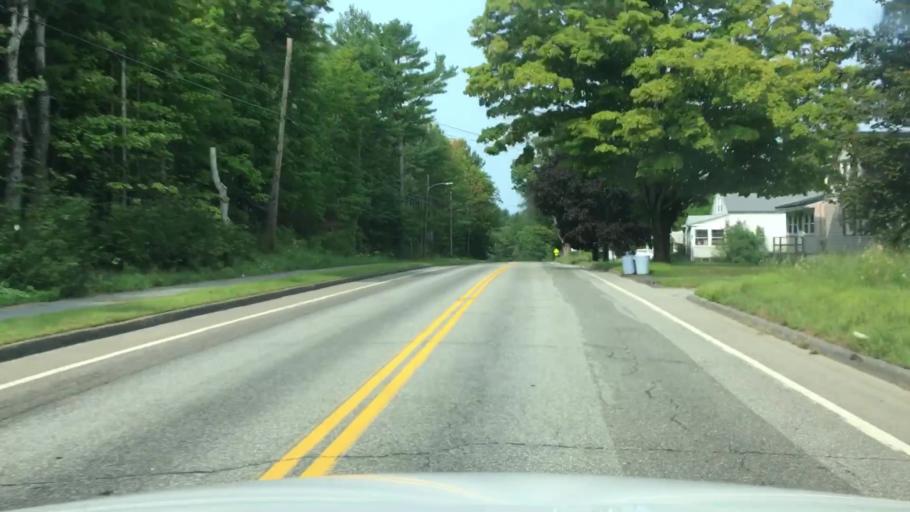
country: US
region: Maine
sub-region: Kennebec County
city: Augusta
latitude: 44.3196
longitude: -69.7477
